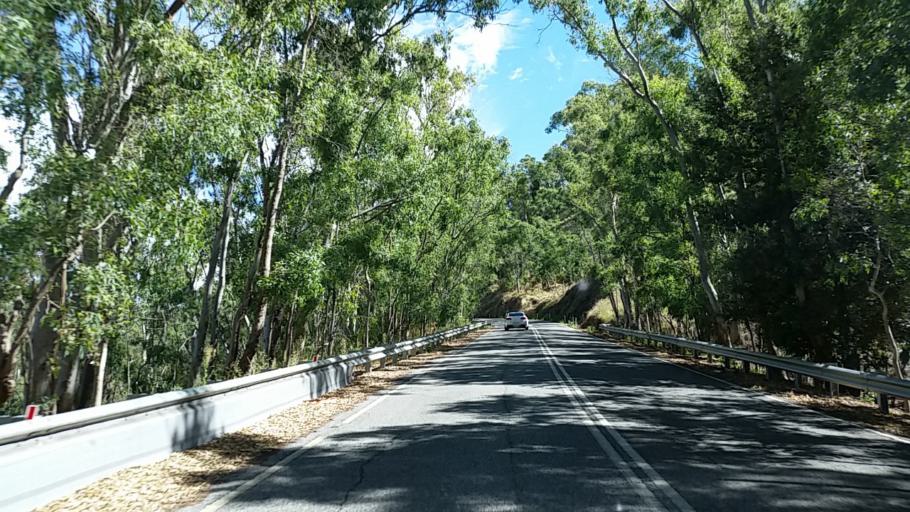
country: AU
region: South Australia
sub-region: Tea Tree Gully
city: Golden Grove
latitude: -34.8530
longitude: 138.7915
